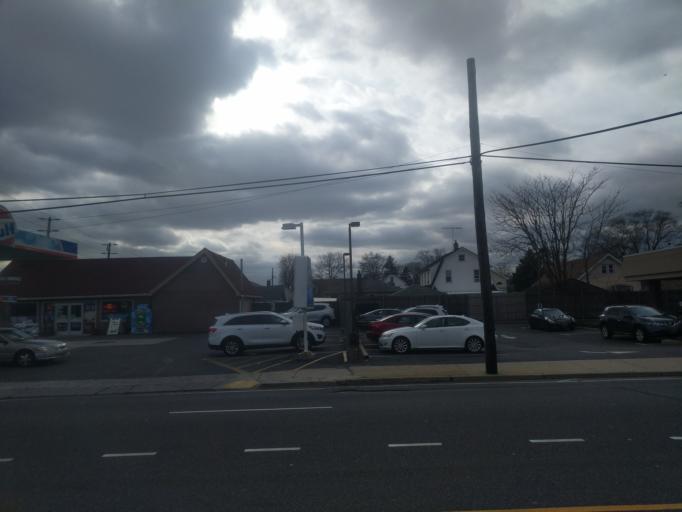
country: US
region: New York
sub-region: Nassau County
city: Lynbrook
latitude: 40.6621
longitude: -73.6883
